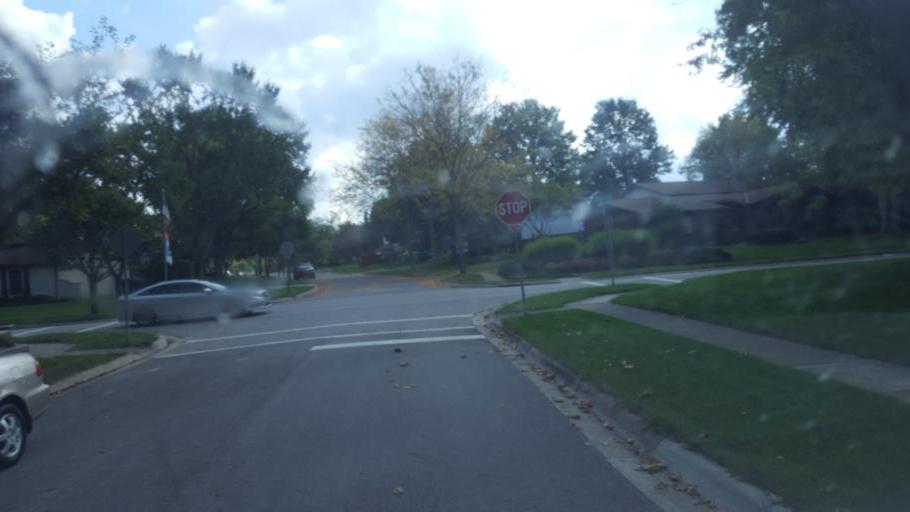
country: US
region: Ohio
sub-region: Franklin County
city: Worthington
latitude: 40.1068
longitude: -83.0282
